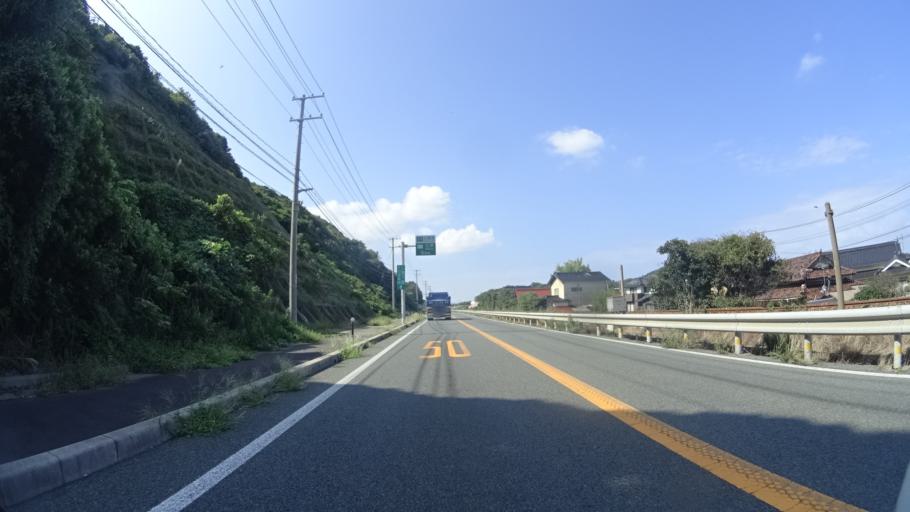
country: JP
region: Shimane
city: Gotsucho
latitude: 35.0334
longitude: 132.2434
